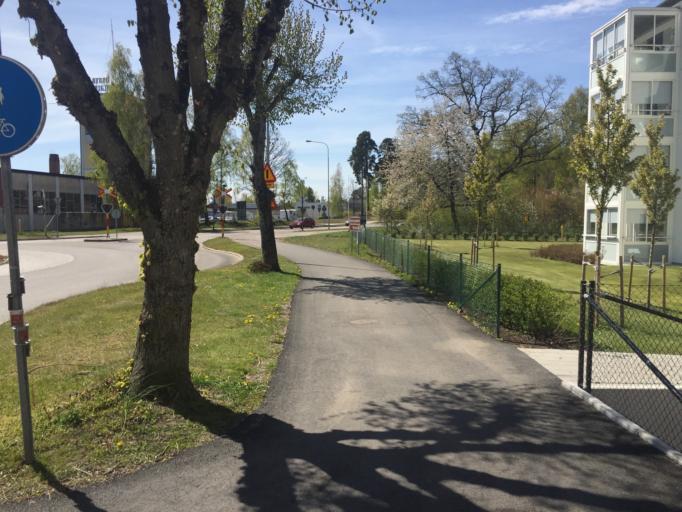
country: SE
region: Kalmar
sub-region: Nybro Kommun
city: Nybro
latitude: 56.7451
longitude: 15.8981
